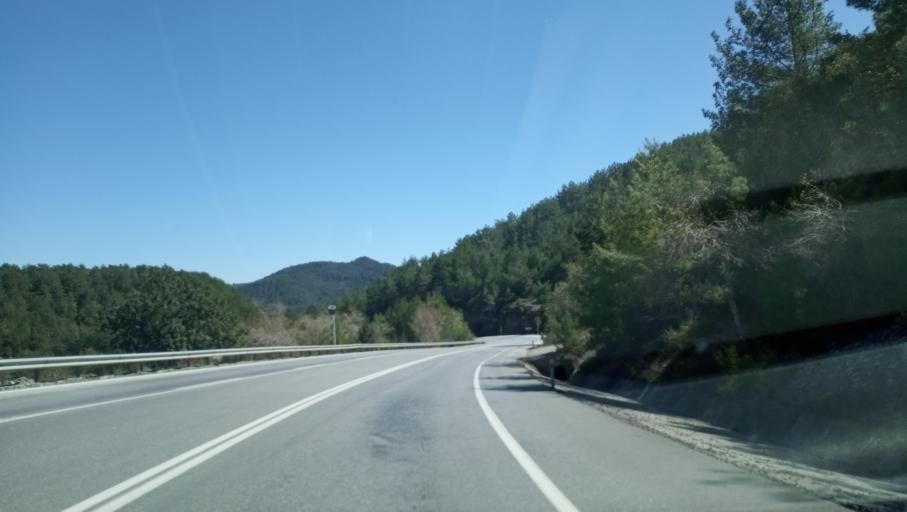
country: TR
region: Antalya
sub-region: Alanya
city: Okurcalar
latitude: 36.7688
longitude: 31.6698
